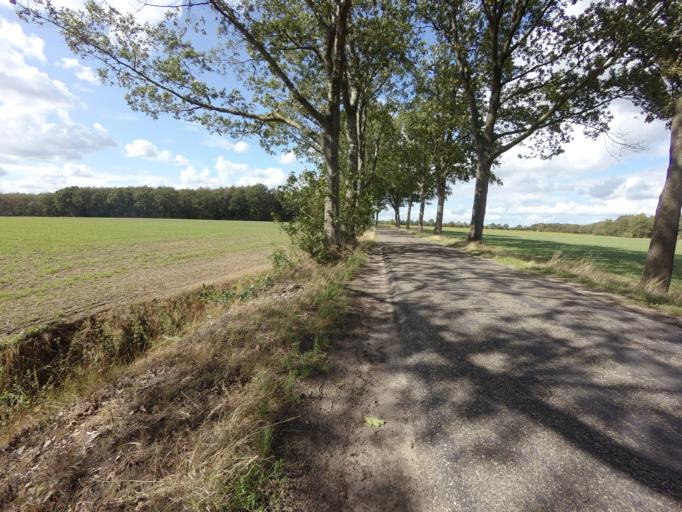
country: NL
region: Friesland
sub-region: Gemeente Heerenveen
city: Jubbega
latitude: 52.9605
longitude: 6.2050
